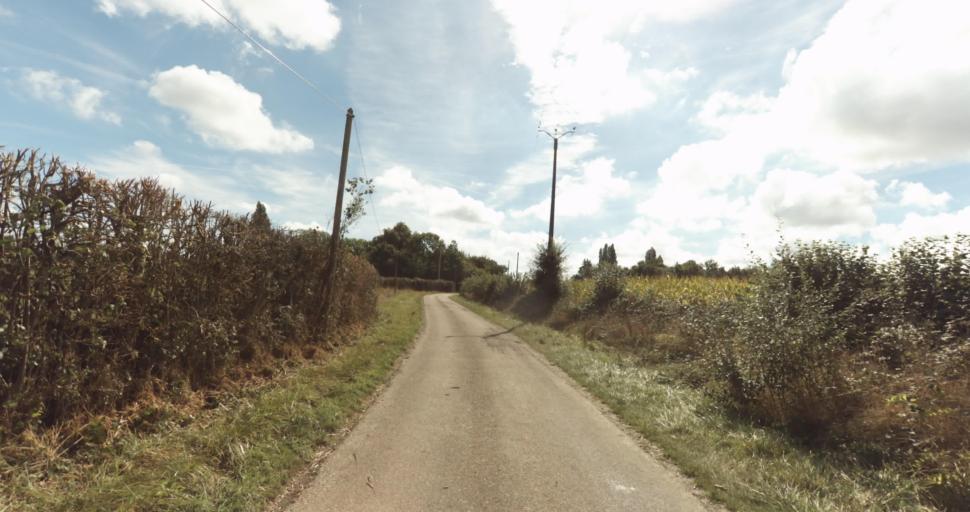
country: FR
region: Lower Normandy
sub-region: Departement du Calvados
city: La Vespiere
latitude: 48.9428
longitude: 0.3231
